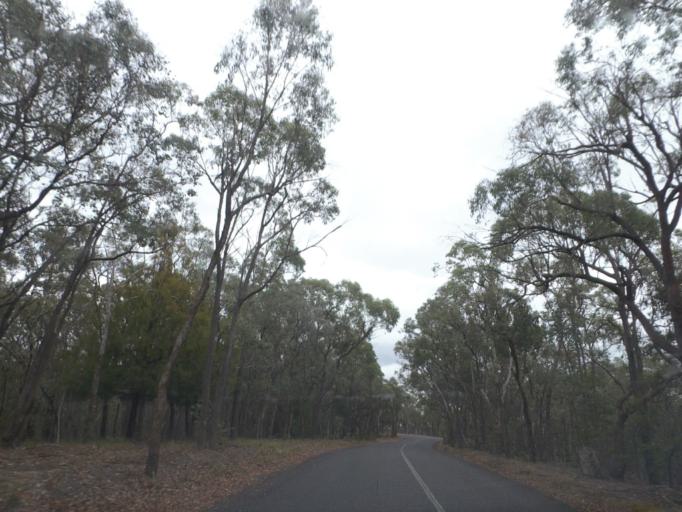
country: AU
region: Victoria
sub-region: Yarra Ranges
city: Yarra Glen
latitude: -37.6406
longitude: 145.3492
